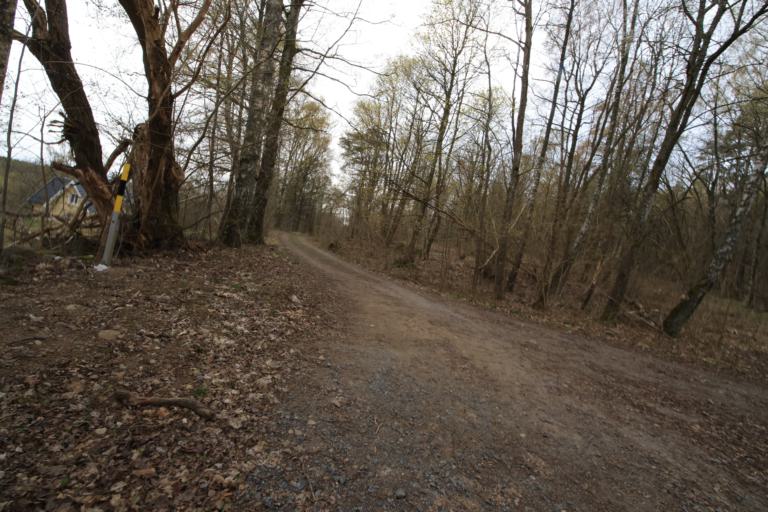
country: SE
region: Halland
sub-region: Varbergs Kommun
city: Tvaaker
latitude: 57.1519
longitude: 12.4629
